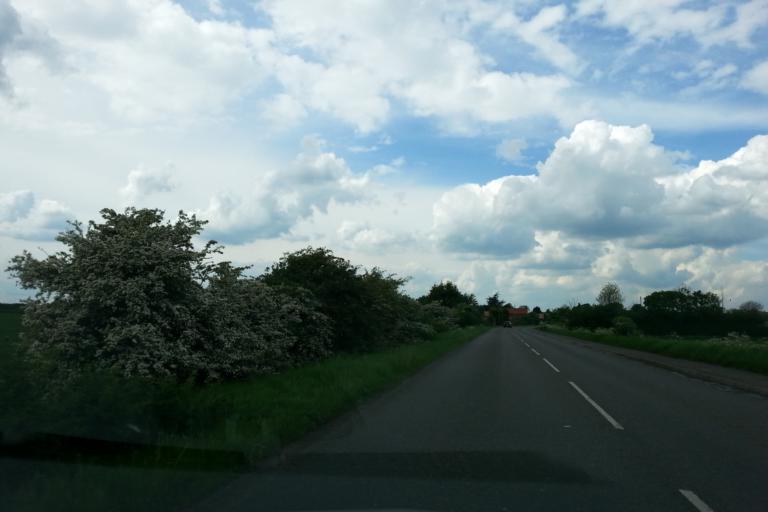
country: GB
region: England
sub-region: Lincolnshire
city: Long Bennington
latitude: 52.9857
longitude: -0.7522
